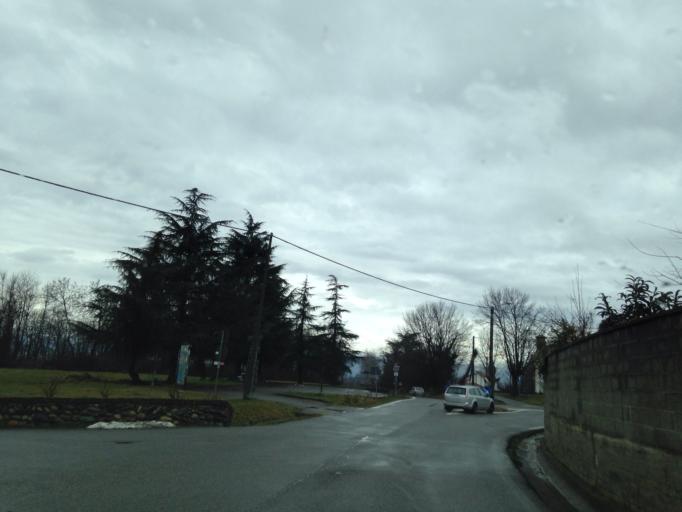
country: IT
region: Piedmont
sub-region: Provincia di Vercelli
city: Moncrivello
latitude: 45.3355
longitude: 7.9946
